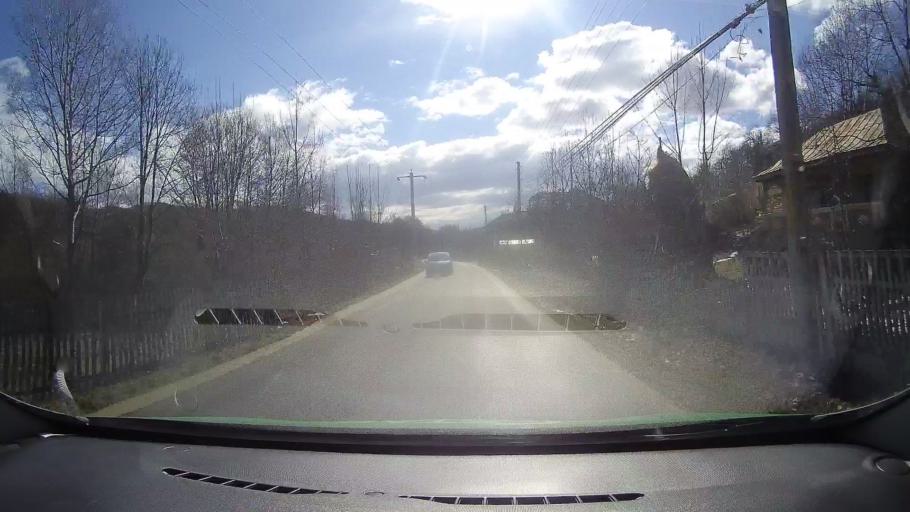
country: RO
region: Dambovita
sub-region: Comuna Runcu
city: Badeni
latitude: 45.1647
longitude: 25.3953
